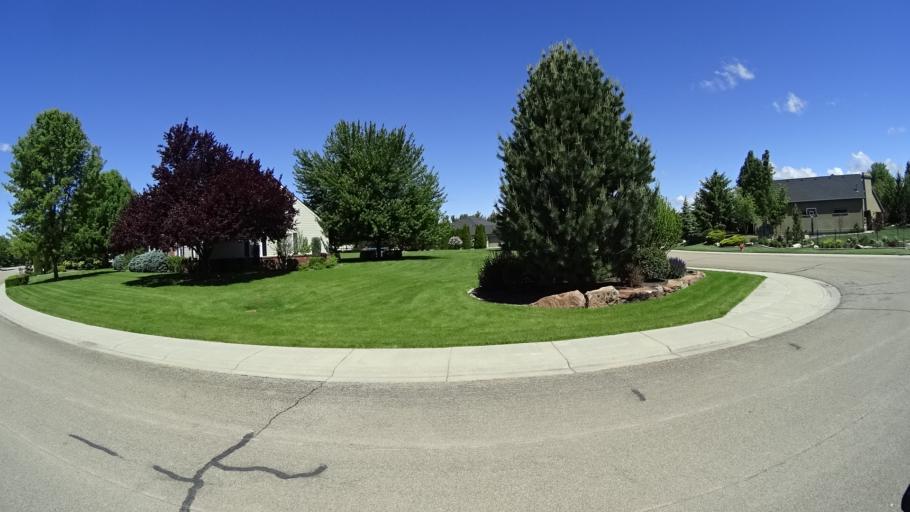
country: US
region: Idaho
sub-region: Ada County
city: Eagle
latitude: 43.6638
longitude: -116.3779
